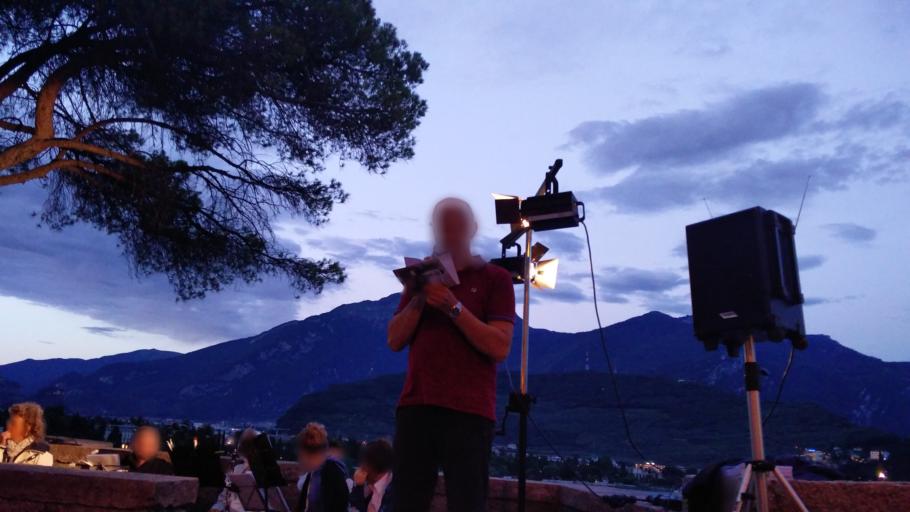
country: IT
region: Trentino-Alto Adige
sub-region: Provincia di Trento
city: Riva del Garda
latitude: 45.8775
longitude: 10.8392
